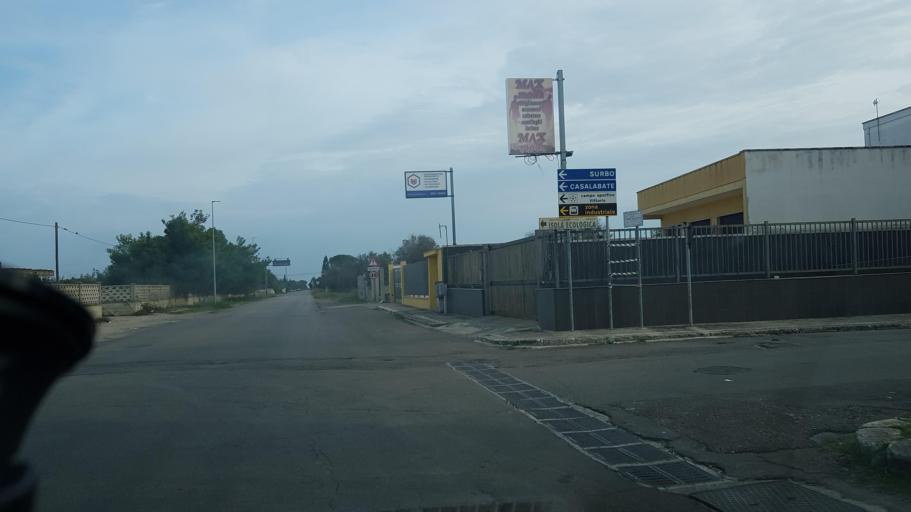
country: IT
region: Apulia
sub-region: Provincia di Lecce
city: Trepuzzi
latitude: 40.3987
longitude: 18.0838
